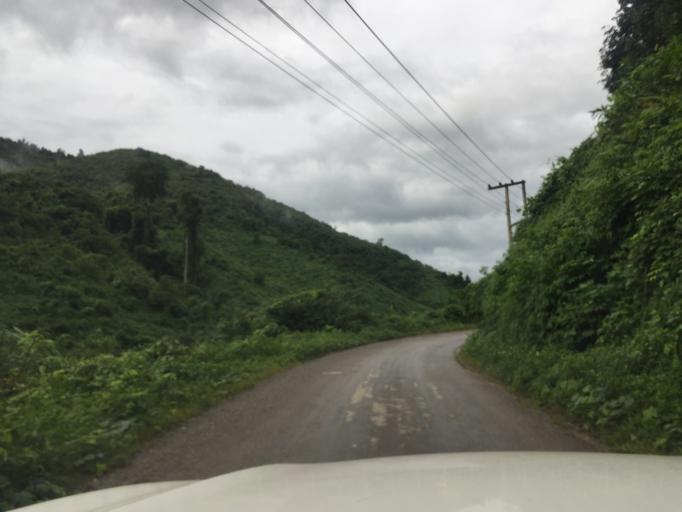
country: LA
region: Oudomxai
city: Muang La
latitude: 21.0268
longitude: 102.2350
